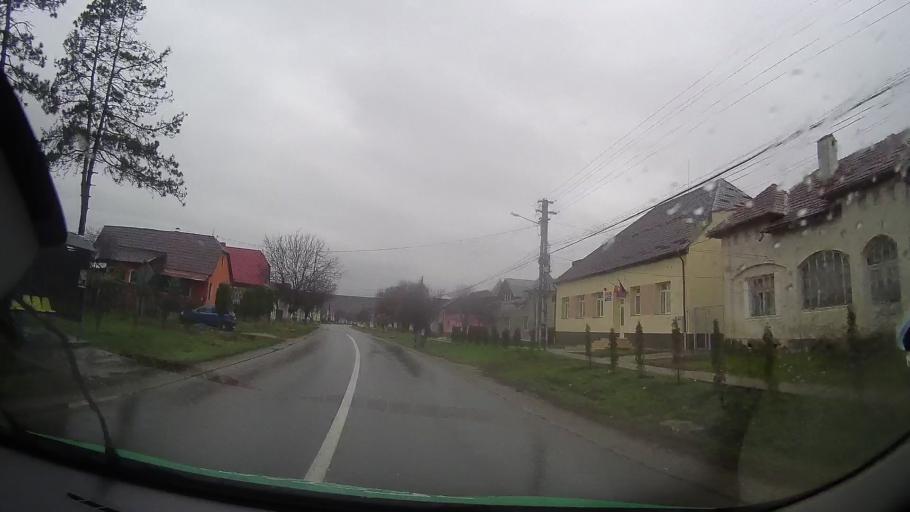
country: RO
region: Bistrita-Nasaud
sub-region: Comuna Mariselu
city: Mariselu
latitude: 47.0366
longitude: 24.4757
